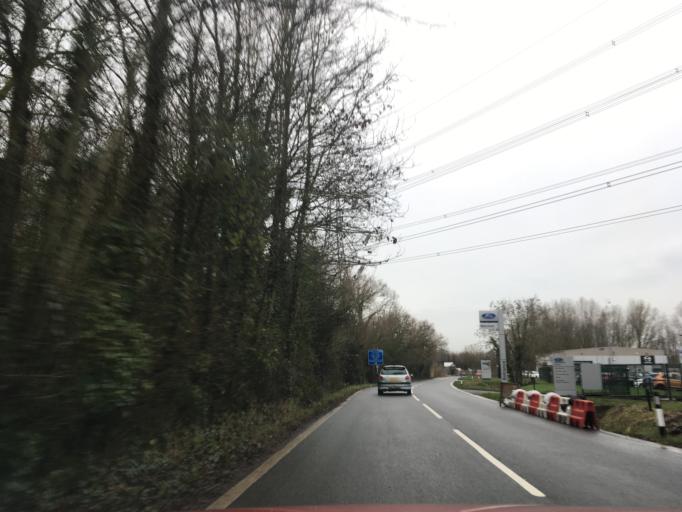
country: GB
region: Wales
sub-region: Newport
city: Nash
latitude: 51.5674
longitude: -2.9510
